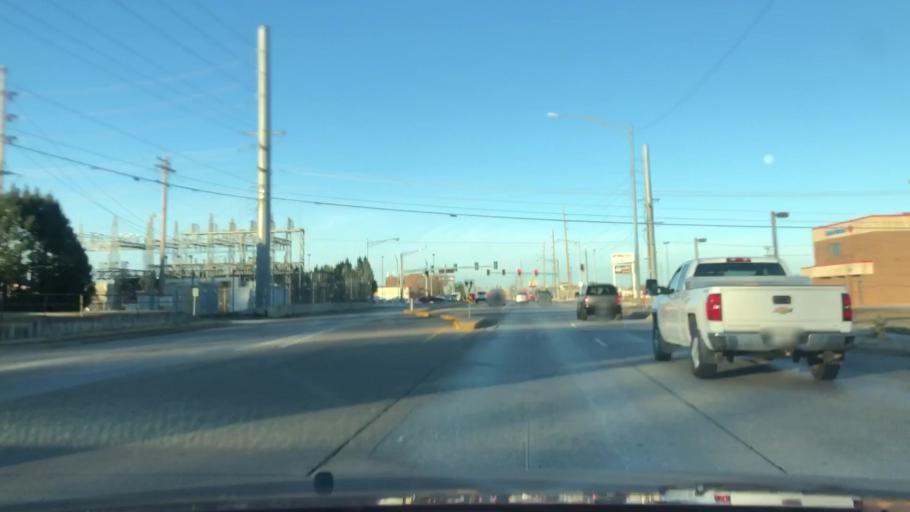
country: US
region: Missouri
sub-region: Greene County
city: Springfield
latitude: 37.1593
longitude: -93.2609
